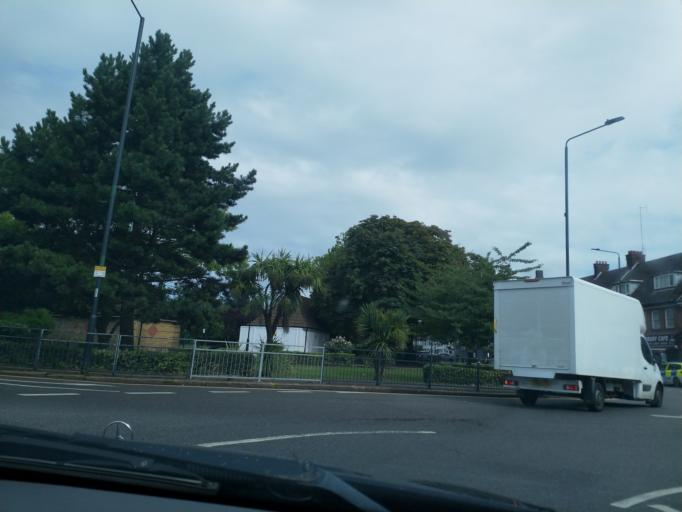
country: GB
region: England
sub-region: Greater London
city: Wembley
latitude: 51.5560
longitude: -0.3171
